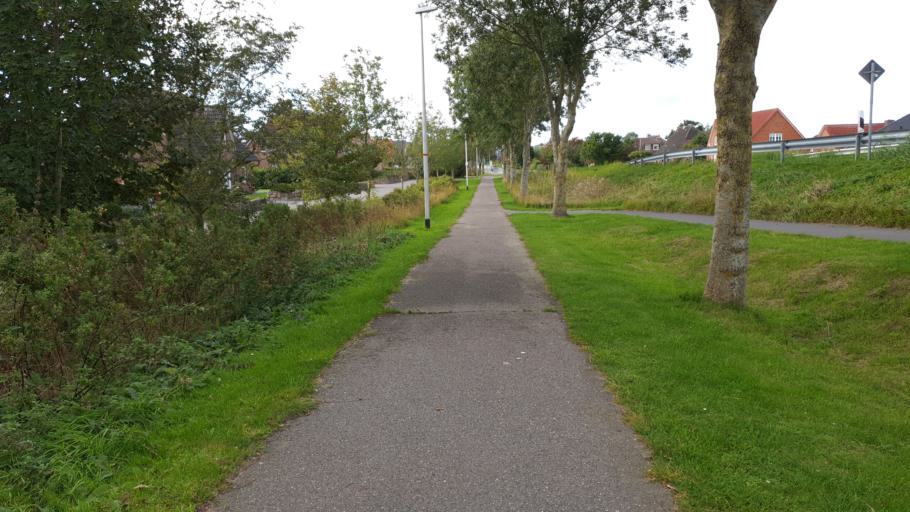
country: DE
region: Schleswig-Holstein
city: Elisabeth-Sophien-Koog
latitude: 54.4881
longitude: 8.8854
